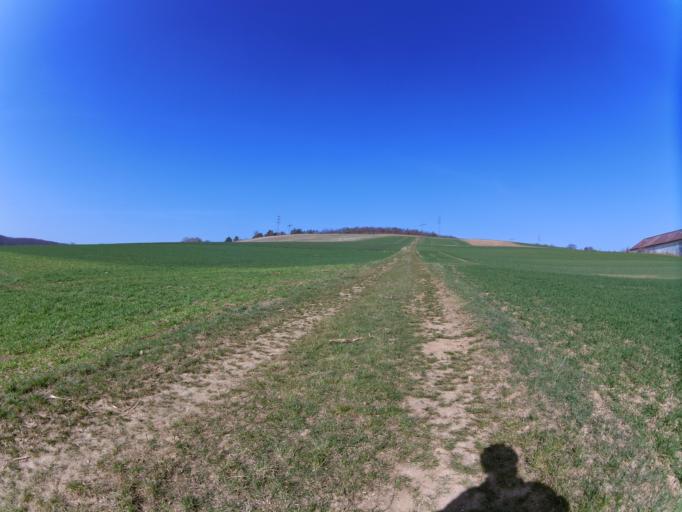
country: DE
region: Bavaria
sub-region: Regierungsbezirk Unterfranken
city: Greussenheim
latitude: 49.8008
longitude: 9.7549
